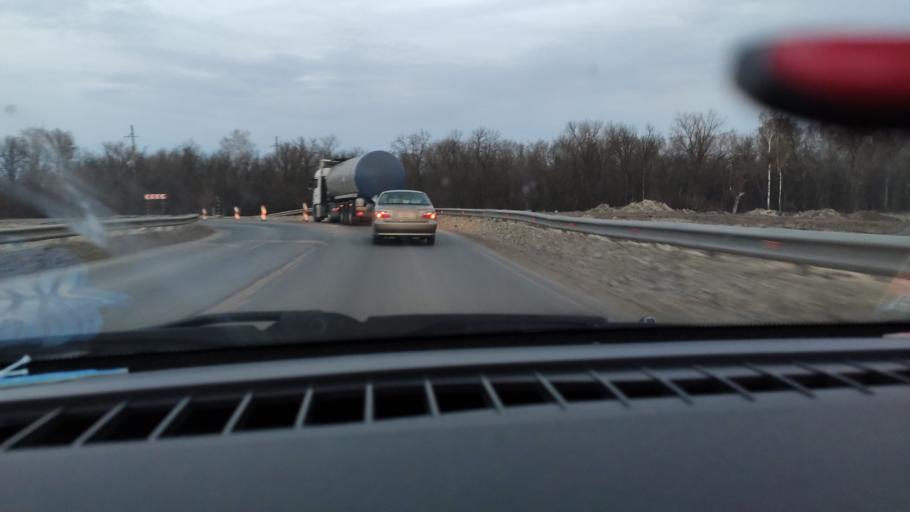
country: RU
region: Saratov
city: Sinodskoye
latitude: 52.0147
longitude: 46.6959
